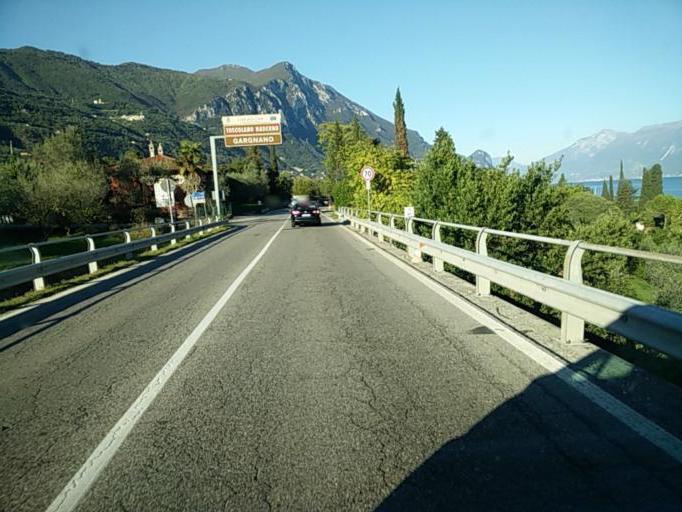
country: IT
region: Lombardy
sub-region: Provincia di Brescia
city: Gargnano
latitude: 45.6689
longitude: 10.6498
